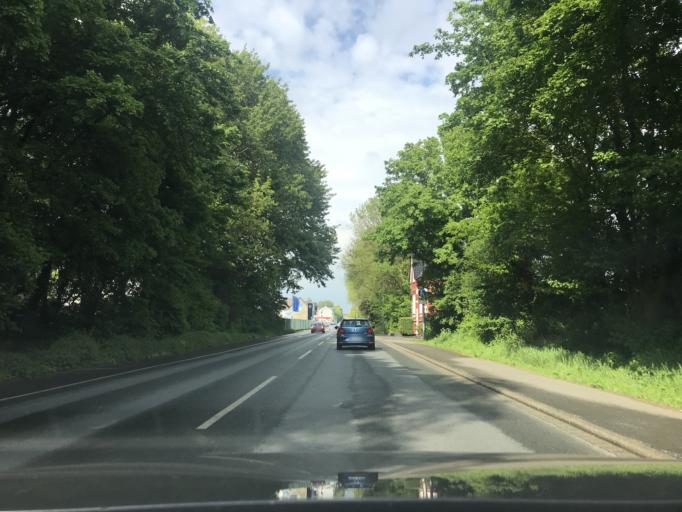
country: DE
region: North Rhine-Westphalia
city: Schwerte
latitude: 51.4300
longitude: 7.5586
